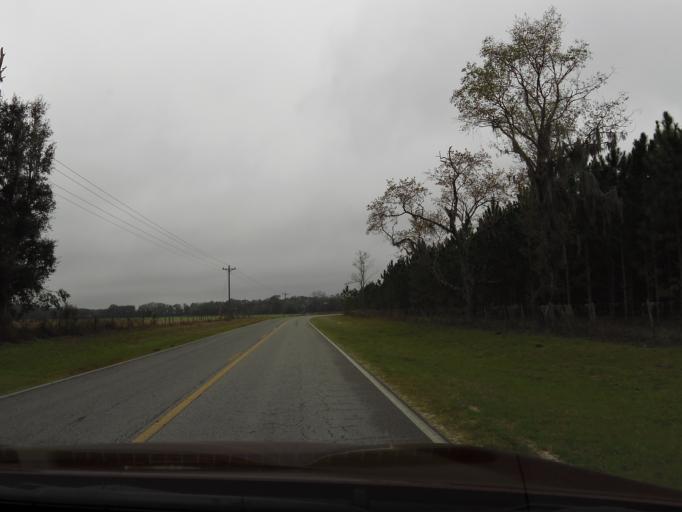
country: US
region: Florida
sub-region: Gilchrist County
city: Trenton
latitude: 29.8024
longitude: -82.9504
